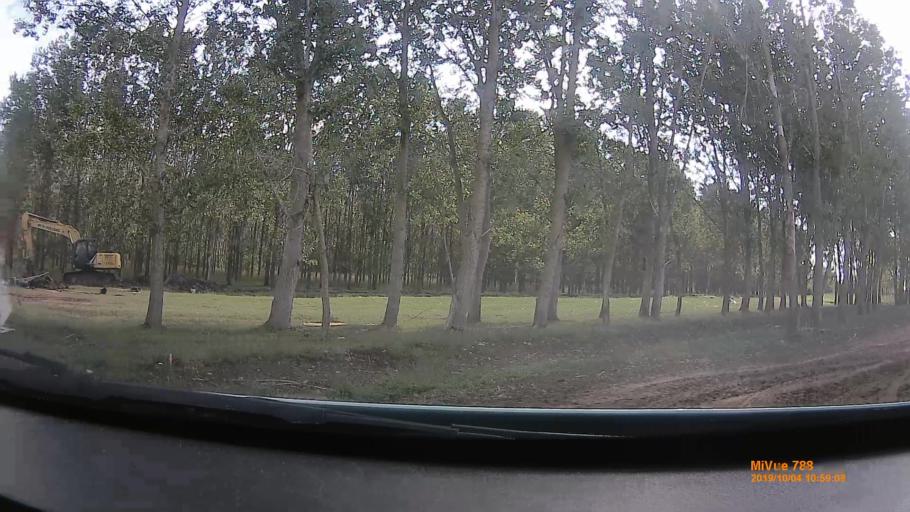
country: HU
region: Szabolcs-Szatmar-Bereg
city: Nyirtelek
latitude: 47.9811
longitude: 21.6667
